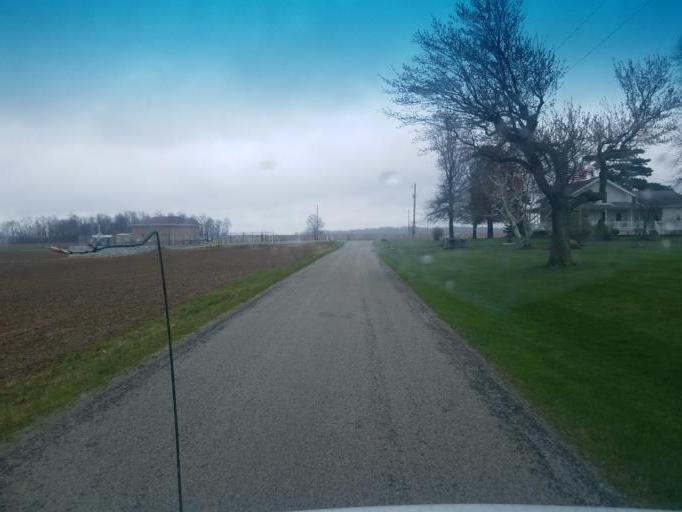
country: US
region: Ohio
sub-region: Huron County
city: Plymouth
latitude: 40.9643
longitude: -82.7260
